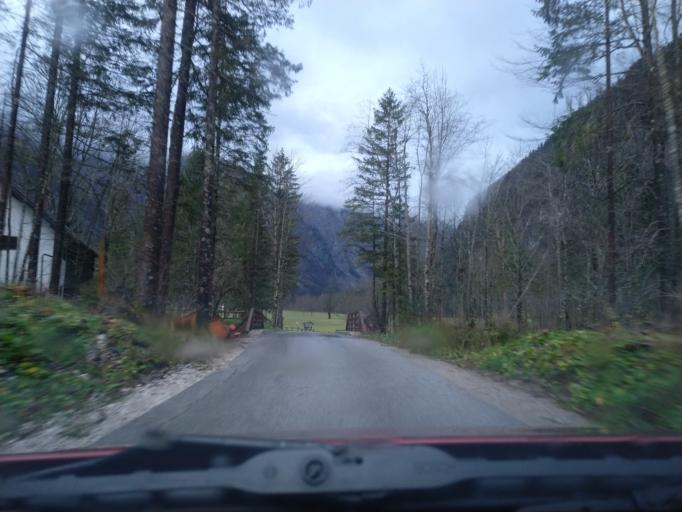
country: SI
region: Solcava
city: Solcava
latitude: 46.3992
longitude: 14.6308
